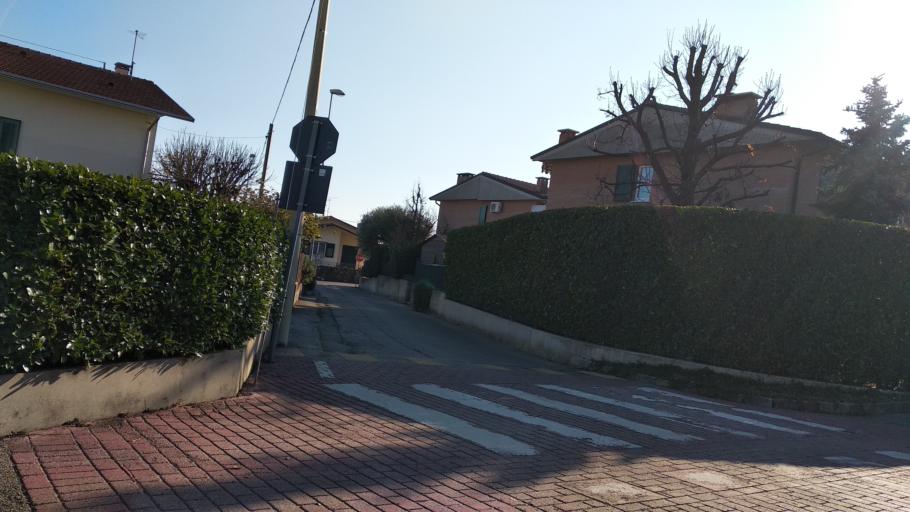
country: IT
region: Veneto
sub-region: Provincia di Vicenza
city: San Vito di Leguzzano
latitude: 45.6993
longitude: 11.3751
